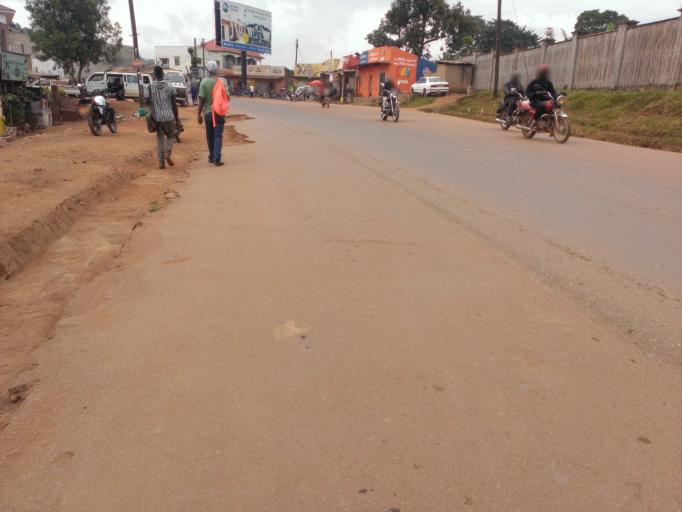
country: UG
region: Central Region
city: Kampala Central Division
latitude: 0.3269
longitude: 32.5576
